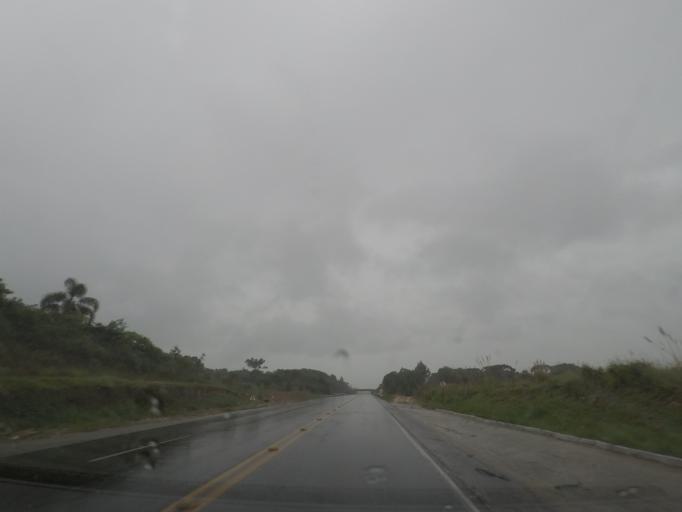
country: BR
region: Parana
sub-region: Almirante Tamandare
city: Almirante Tamandare
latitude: -25.3614
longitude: -49.3147
